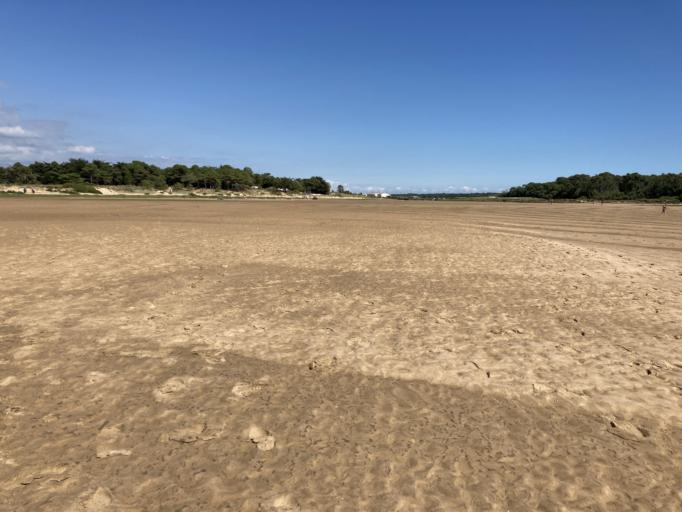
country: FR
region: Pays de la Loire
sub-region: Departement de la Vendee
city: Saint-Hilaire-de-Talmont
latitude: 46.4345
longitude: -1.6441
